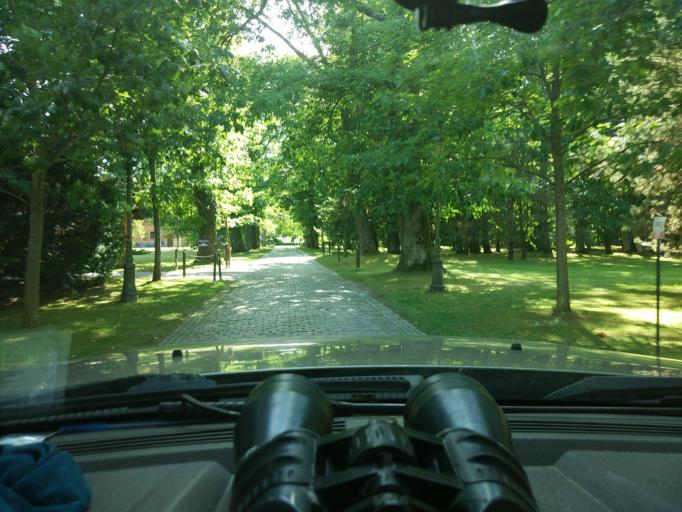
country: PL
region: Pomeranian Voivodeship
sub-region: Powiat wejherowski
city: Choczewo
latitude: 54.7467
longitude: 17.7979
